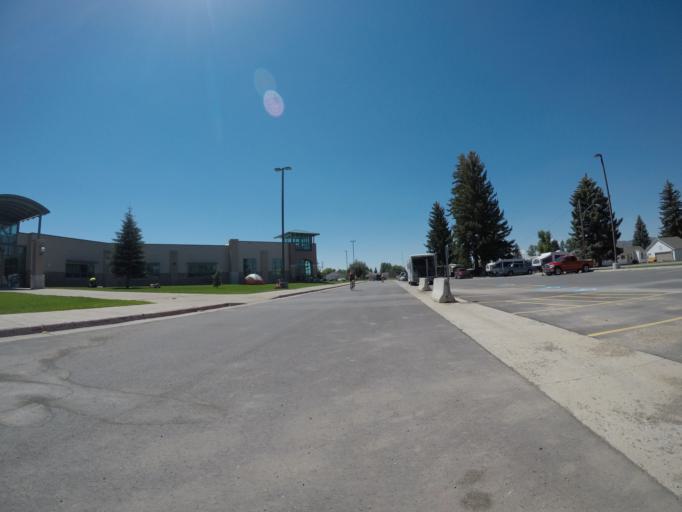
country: US
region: Idaho
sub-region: Bear Lake County
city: Montpelier
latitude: 42.0833
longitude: -110.9560
